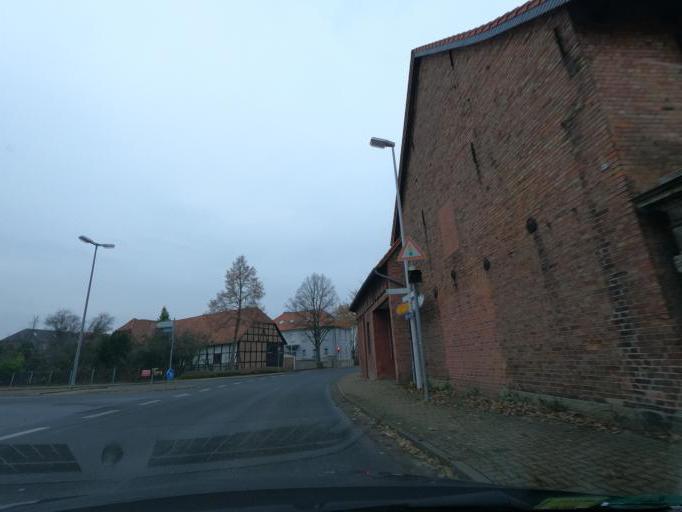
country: DE
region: Lower Saxony
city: Wolfenbuettel
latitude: 52.1952
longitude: 10.5859
